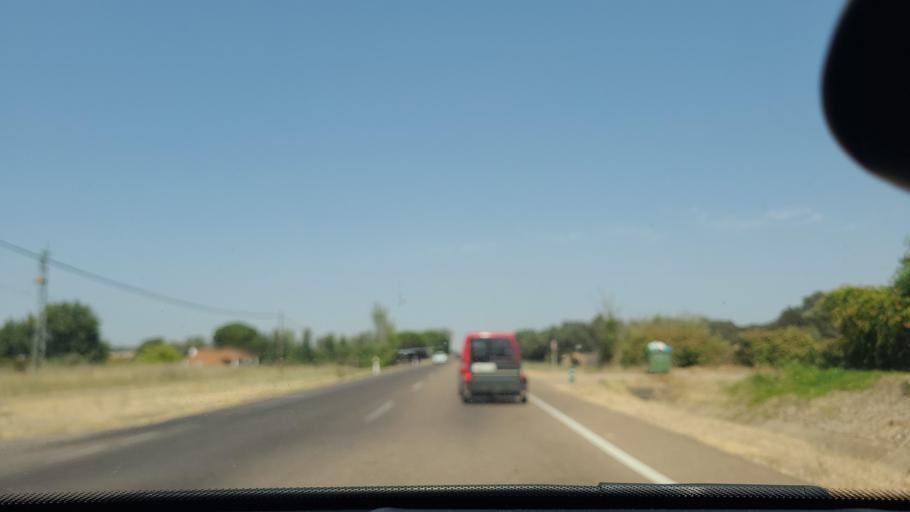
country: ES
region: Extremadura
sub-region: Provincia de Badajoz
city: Badajoz
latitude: 38.8319
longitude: -6.9192
